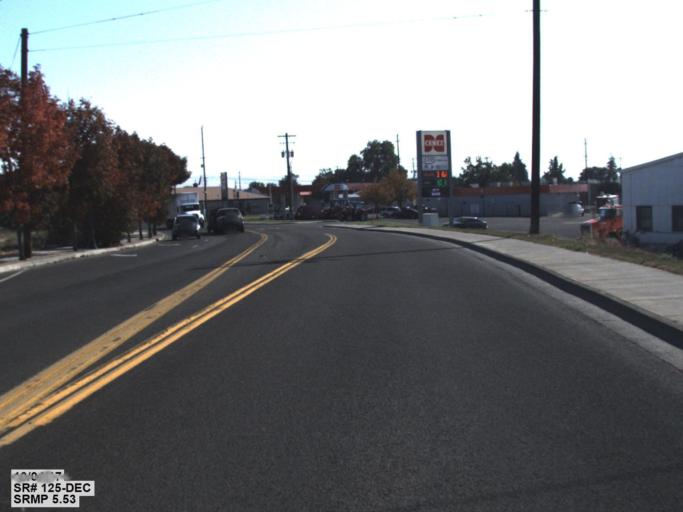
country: US
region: Washington
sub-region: Walla Walla County
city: Walla Walla
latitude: 46.0656
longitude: -118.3499
